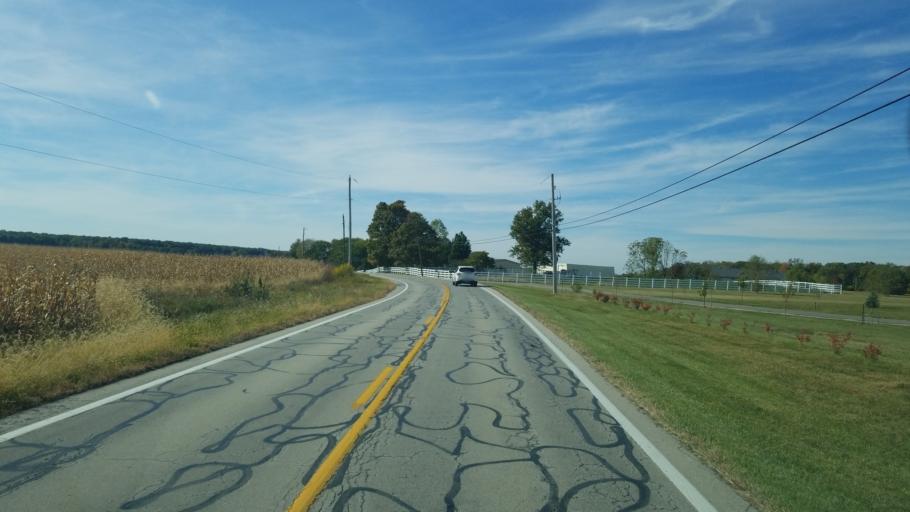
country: US
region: Ohio
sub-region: Clinton County
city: Wilmington
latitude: 39.3736
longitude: -83.9008
